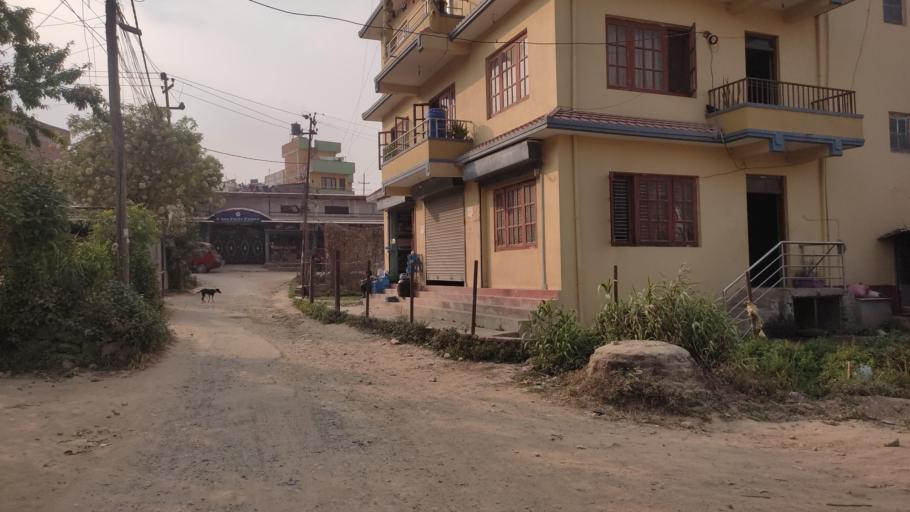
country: NP
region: Central Region
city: Kirtipur
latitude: 27.6715
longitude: 85.2771
